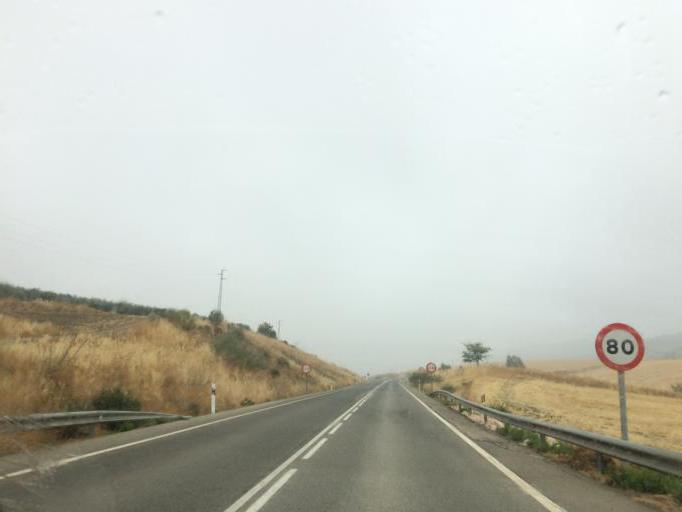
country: ES
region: Andalusia
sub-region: Provincia de Malaga
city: Casabermeja
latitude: 36.9008
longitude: -4.4214
